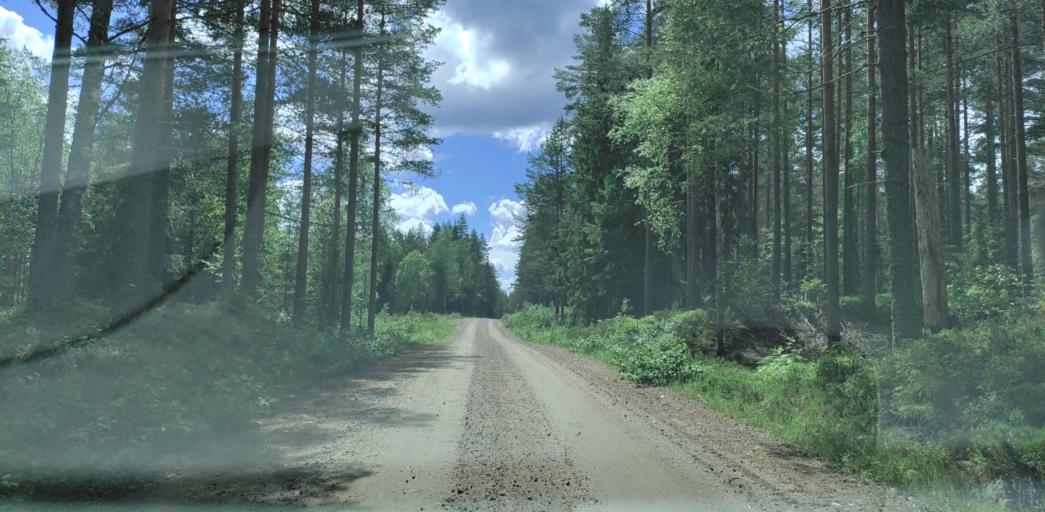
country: SE
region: Vaermland
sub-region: Hagfors Kommun
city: Ekshaerad
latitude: 60.0709
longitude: 13.3101
